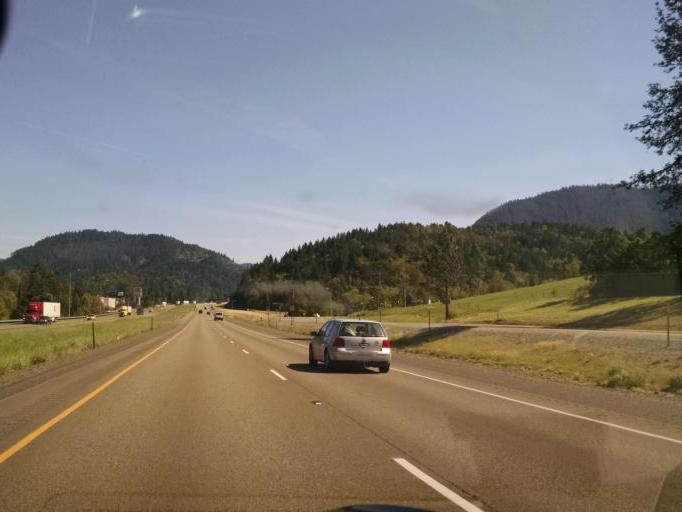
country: US
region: Oregon
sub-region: Douglas County
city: Canyonville
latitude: 42.9453
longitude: -123.2932
